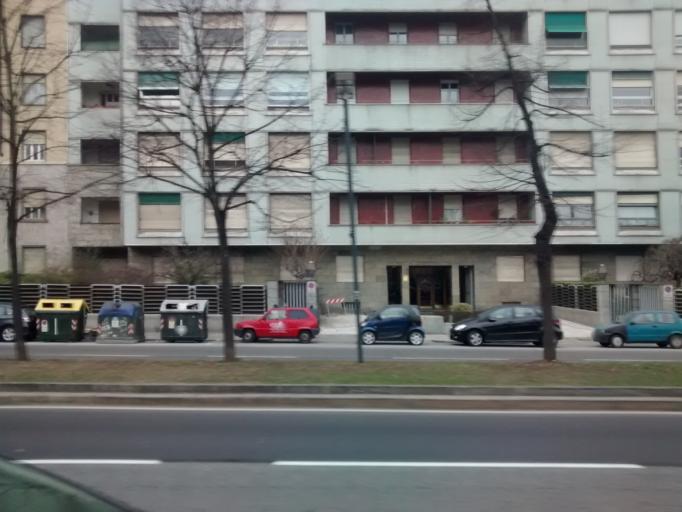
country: IT
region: Piedmont
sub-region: Provincia di Torino
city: Turin
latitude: 45.0577
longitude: 7.6866
